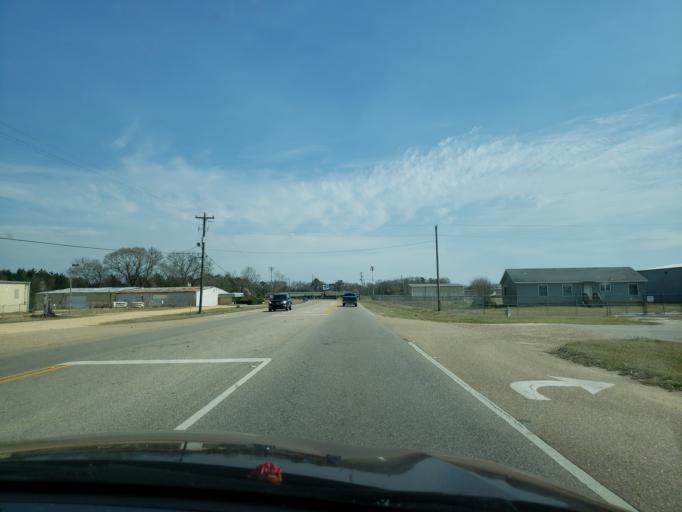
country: US
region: Alabama
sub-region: Elmore County
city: Elmore
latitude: 32.5312
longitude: -86.3291
